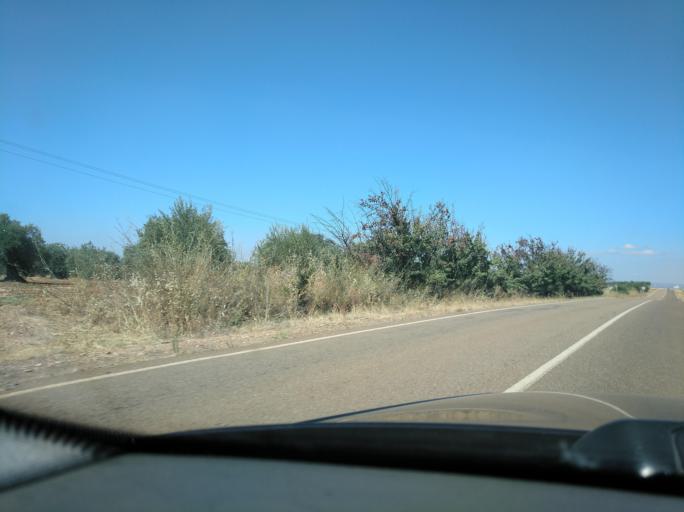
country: ES
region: Extremadura
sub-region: Provincia de Badajoz
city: Olivenza
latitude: 38.6910
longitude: -7.1162
